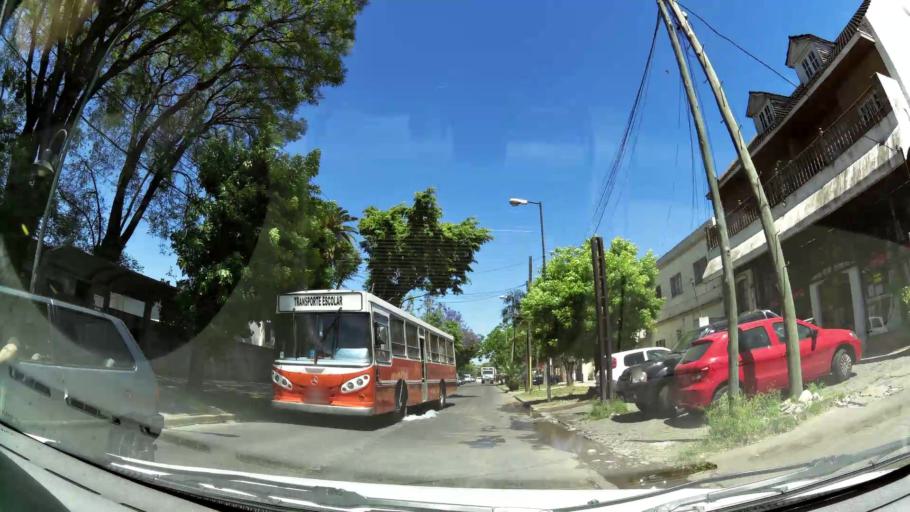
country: AR
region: Buenos Aires
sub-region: Partido de Vicente Lopez
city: Olivos
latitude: -34.5142
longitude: -58.5308
